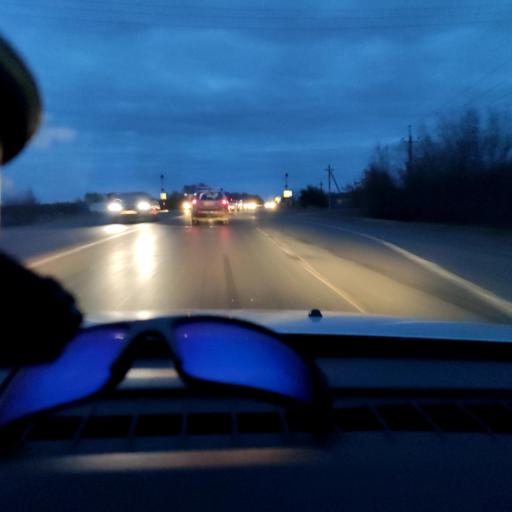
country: RU
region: Samara
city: Novokuybyshevsk
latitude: 53.0849
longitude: 50.0656
